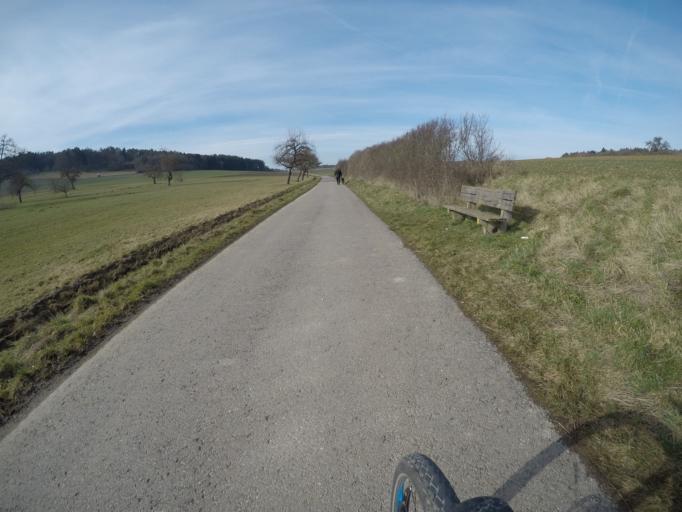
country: DE
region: Baden-Wuerttemberg
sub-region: Karlsruhe Region
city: Gechingen
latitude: 48.6956
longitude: 8.8086
